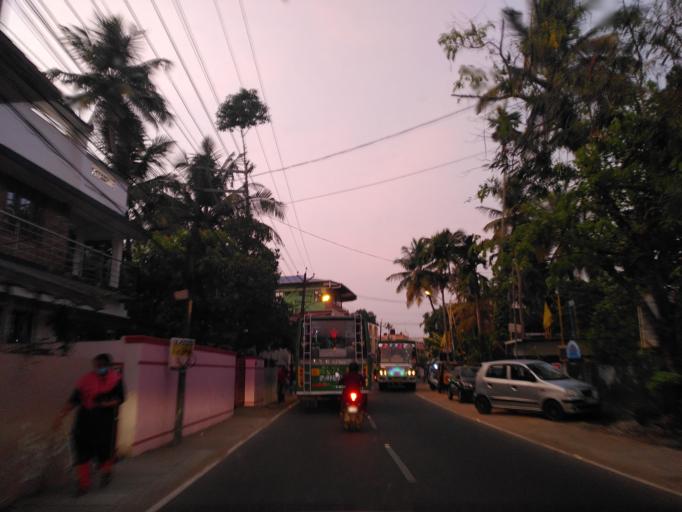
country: IN
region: Kerala
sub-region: Ernakulam
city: Cochin
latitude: 9.9064
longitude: 76.2806
